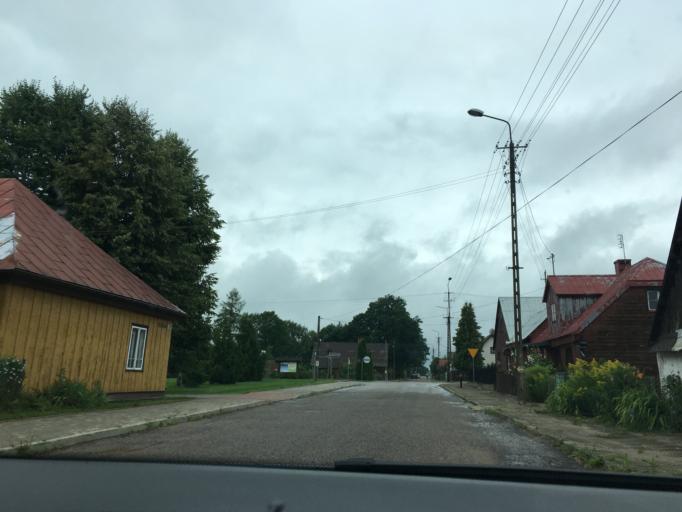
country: PL
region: Podlasie
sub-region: Powiat sejnenski
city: Krasnopol
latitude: 54.1153
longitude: 23.2073
